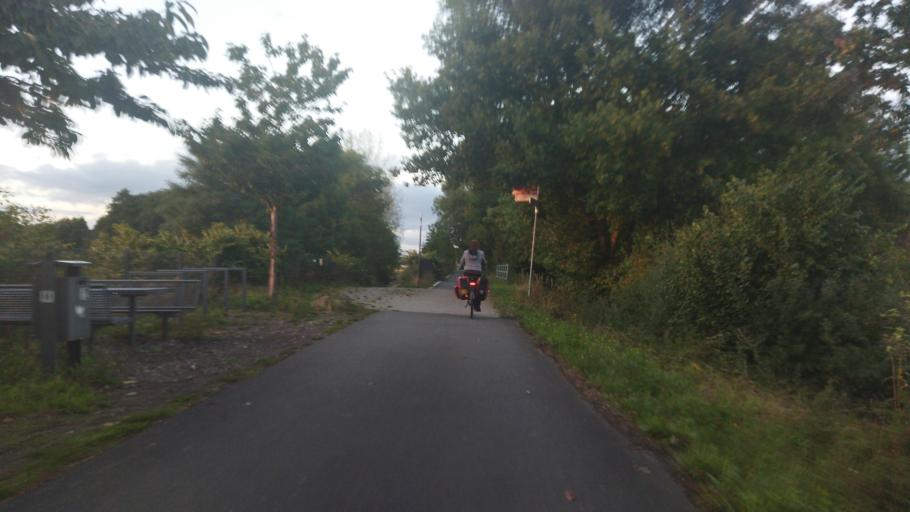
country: DE
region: North Rhine-Westphalia
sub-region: Regierungsbezirk Munster
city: Horstmar
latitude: 52.0343
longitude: 7.3055
